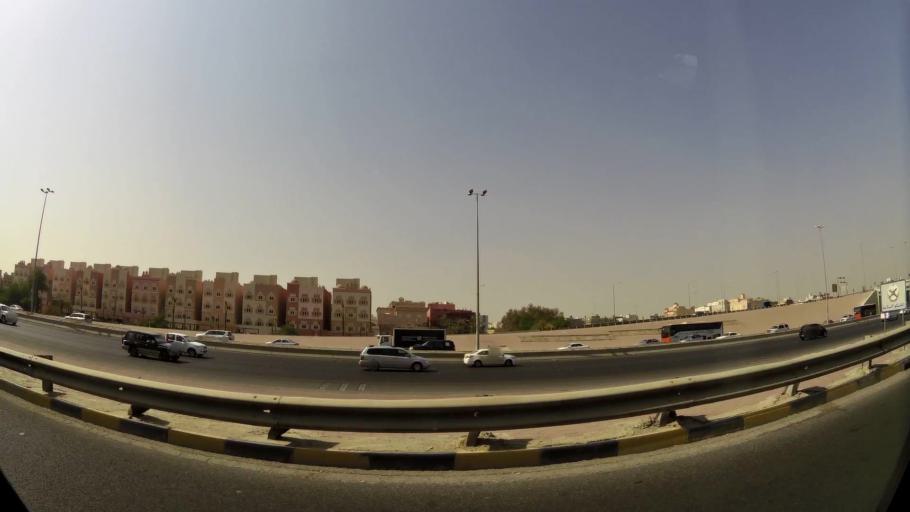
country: KW
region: Al Ahmadi
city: Al Fintas
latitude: 29.1830
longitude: 48.1128
